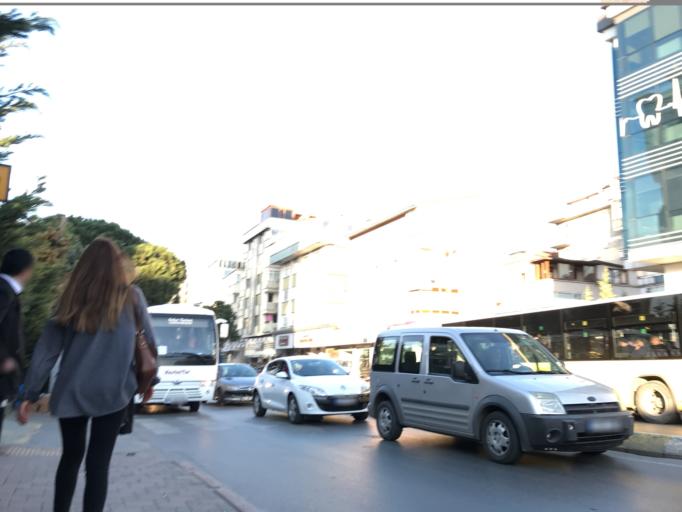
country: TR
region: Istanbul
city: Maltepe
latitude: 40.9320
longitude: 29.1359
